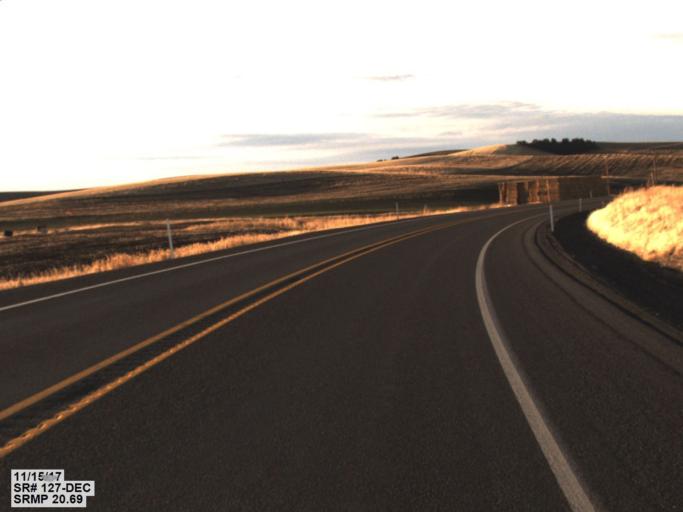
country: US
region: Washington
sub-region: Garfield County
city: Pomeroy
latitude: 46.7390
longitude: -117.7306
